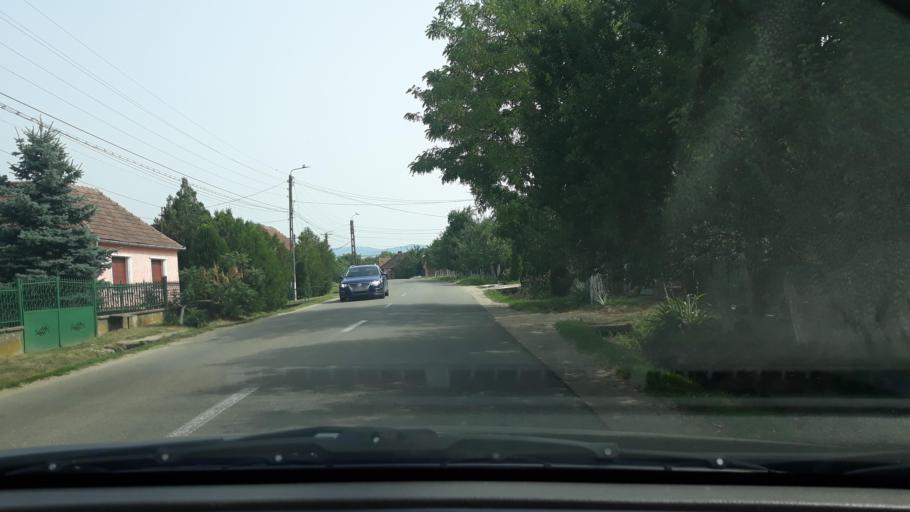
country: RO
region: Bihor
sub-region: Comuna Tauteu
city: Tauteu
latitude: 47.2756
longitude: 22.3294
